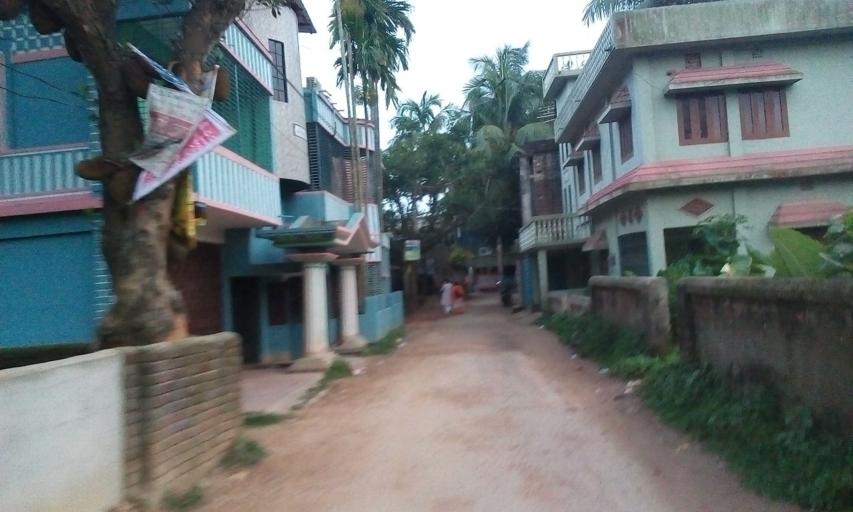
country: IN
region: West Bengal
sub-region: Dakshin Dinajpur
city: Balurghat
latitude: 25.3850
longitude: 88.9936
